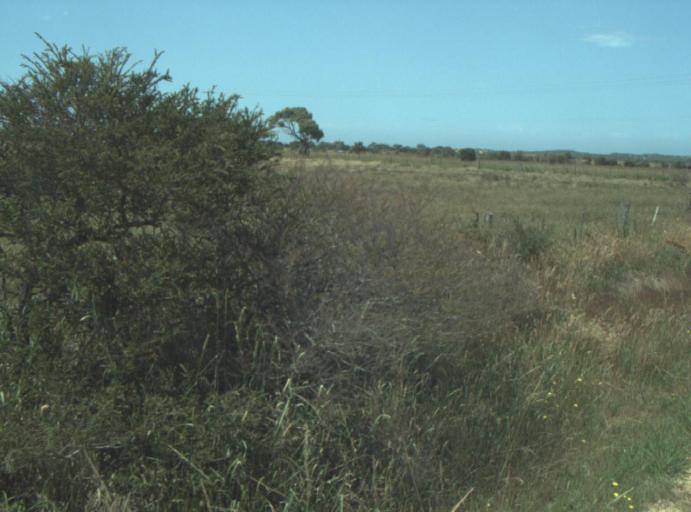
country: AU
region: Victoria
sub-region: Greater Geelong
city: Breakwater
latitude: -38.2649
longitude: 144.4046
